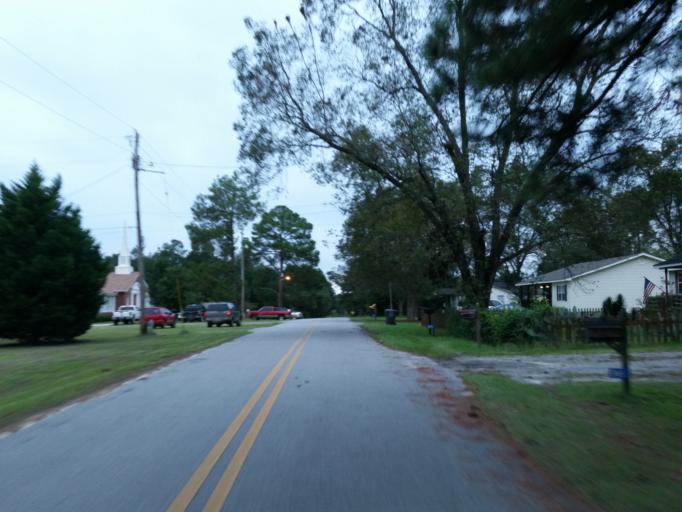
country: US
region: Georgia
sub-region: Crisp County
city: Cordele
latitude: 31.8340
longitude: -83.7424
